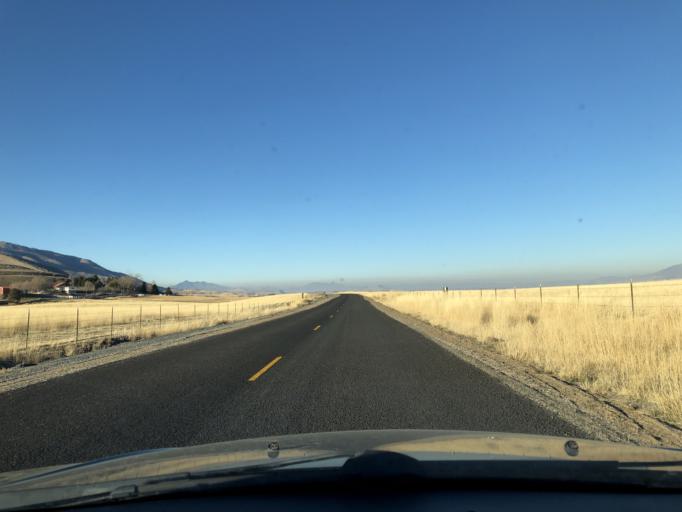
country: US
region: Utah
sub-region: Cache County
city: Wellsville
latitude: 41.5903
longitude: -111.9266
